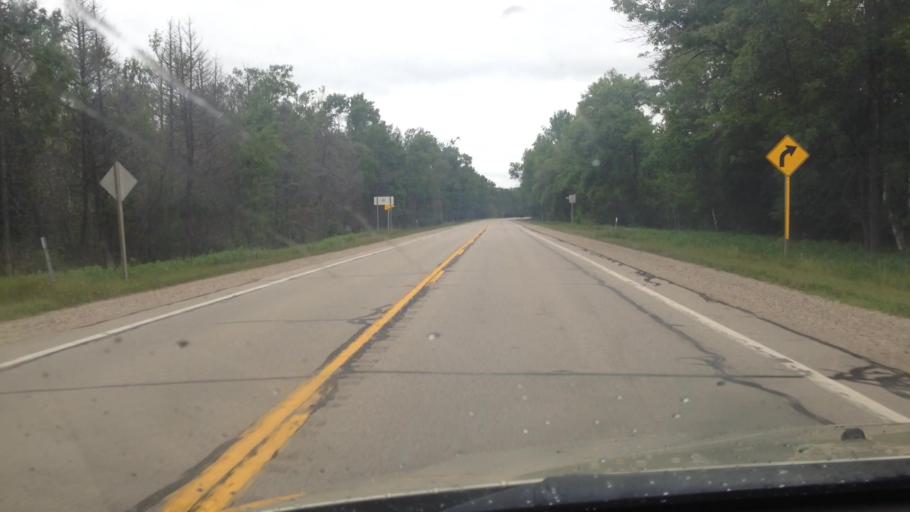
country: US
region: Michigan
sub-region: Menominee County
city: Menominee
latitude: 45.4224
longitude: -87.3484
